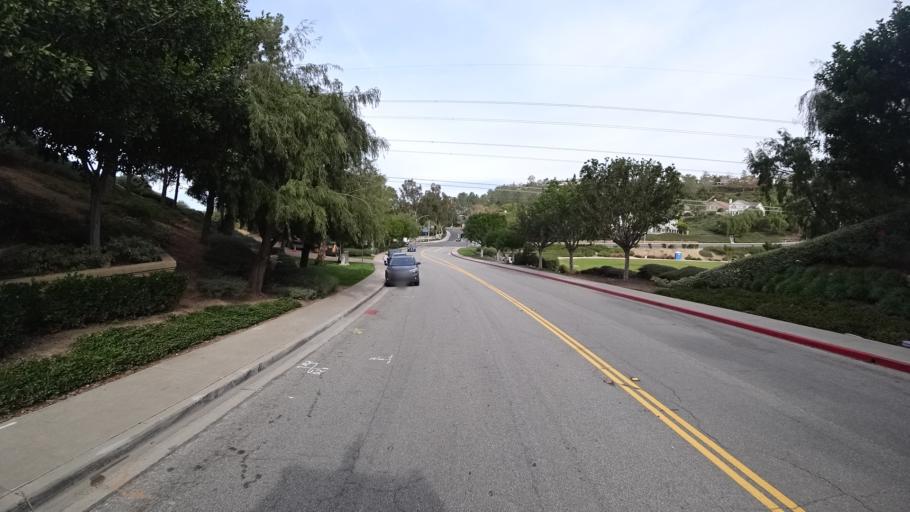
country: US
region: California
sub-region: Orange County
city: Laguna Woods
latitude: 33.5951
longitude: -117.7388
